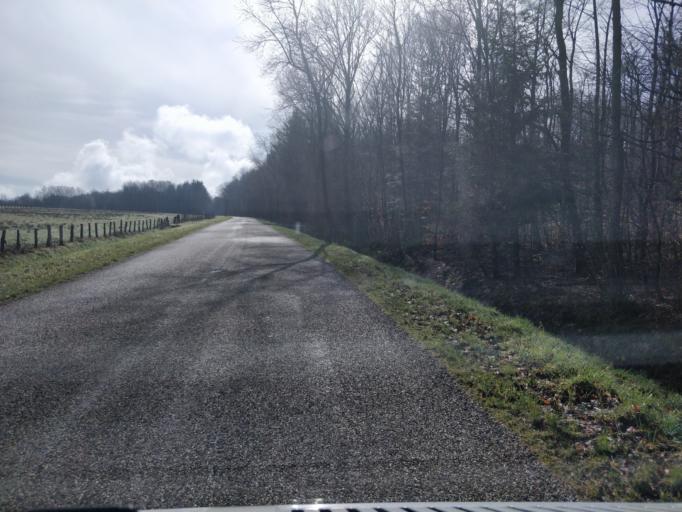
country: FR
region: Alsace
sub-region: Departement du Bas-Rhin
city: Drulingen
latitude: 48.8869
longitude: 7.2601
